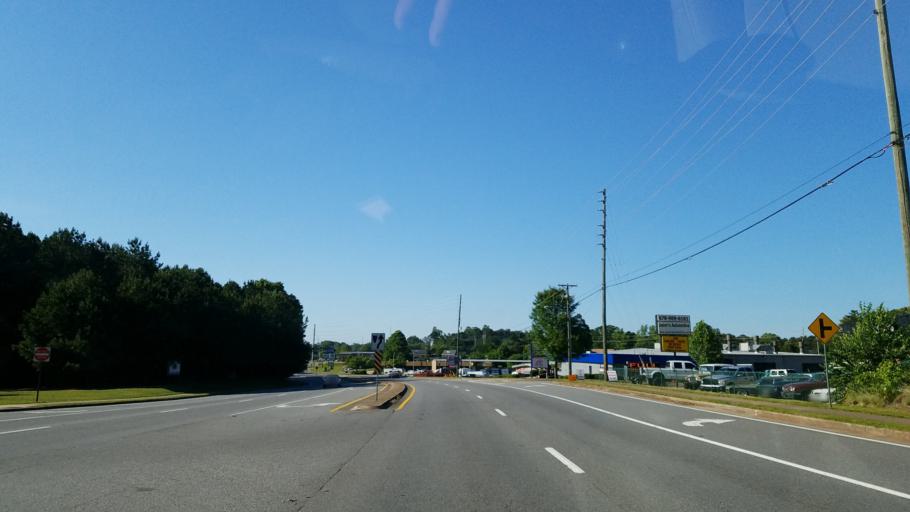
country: US
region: Georgia
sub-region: Cherokee County
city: Woodstock
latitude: 34.1023
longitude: -84.5806
